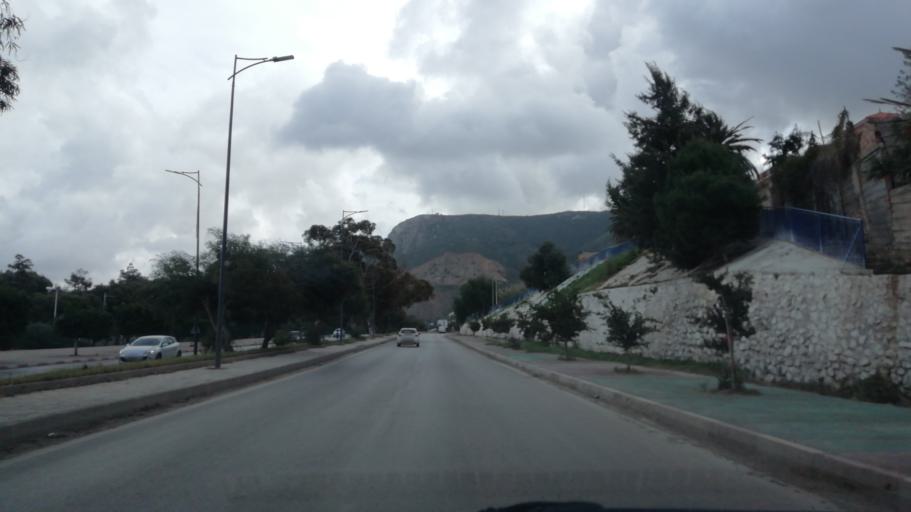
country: DZ
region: Oran
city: Mers el Kebir
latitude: 35.7169
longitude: -0.6961
